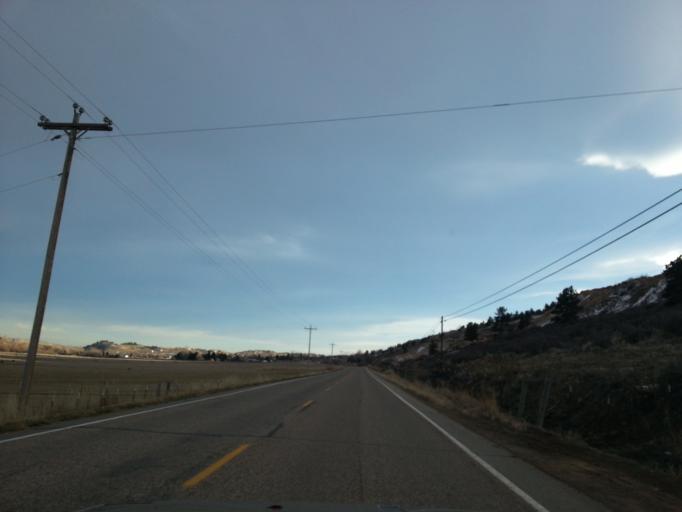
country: US
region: Colorado
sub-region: Larimer County
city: Loveland
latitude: 40.4477
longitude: -105.2033
